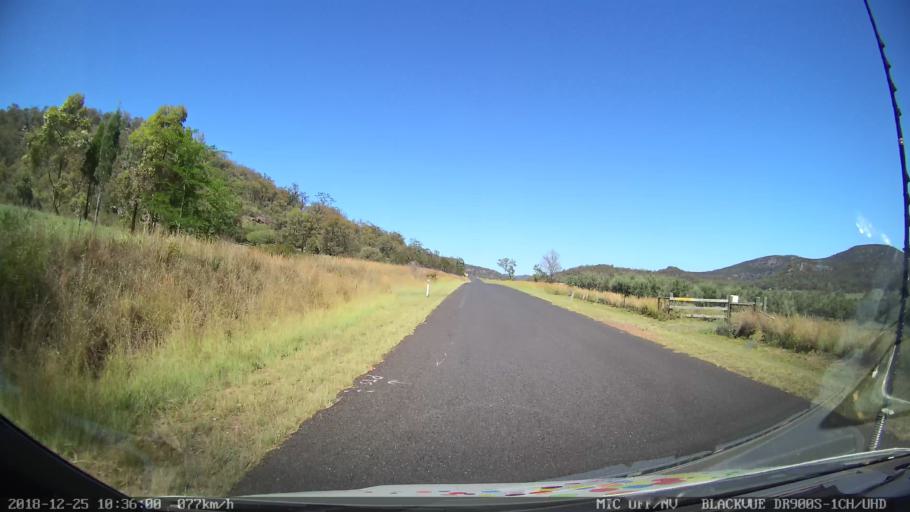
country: AU
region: New South Wales
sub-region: Upper Hunter Shire
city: Merriwa
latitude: -32.4020
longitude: 150.3902
